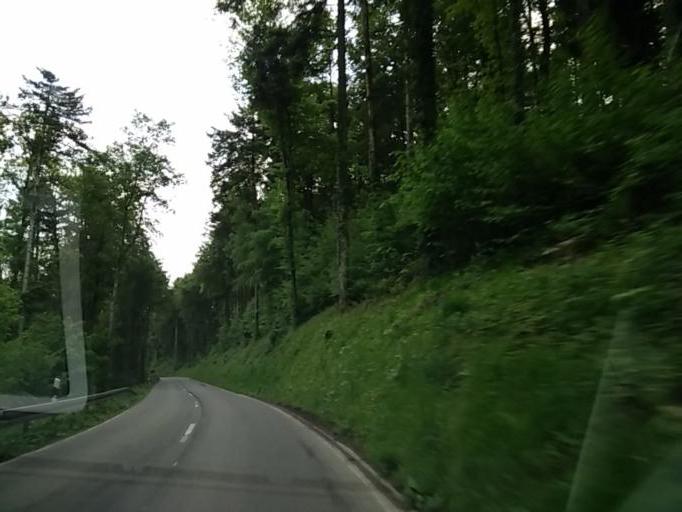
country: DE
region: Baden-Wuerttemberg
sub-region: Tuebingen Region
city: Hirrlingen
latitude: 48.4248
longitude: 8.8605
